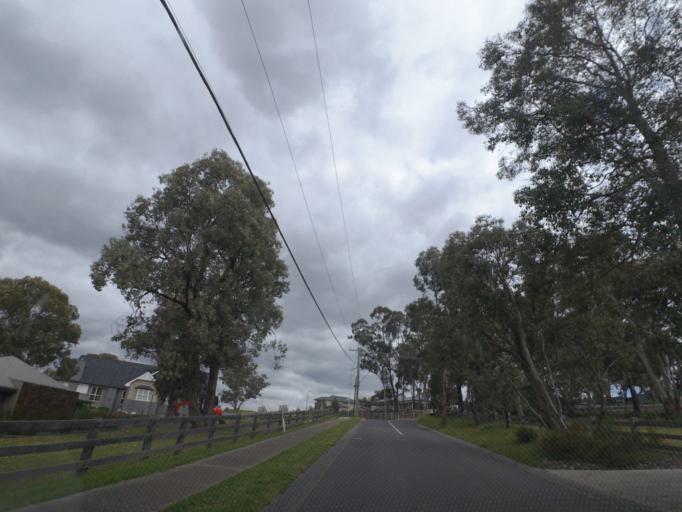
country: AU
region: Victoria
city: Plenty
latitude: -37.6648
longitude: 145.1167
